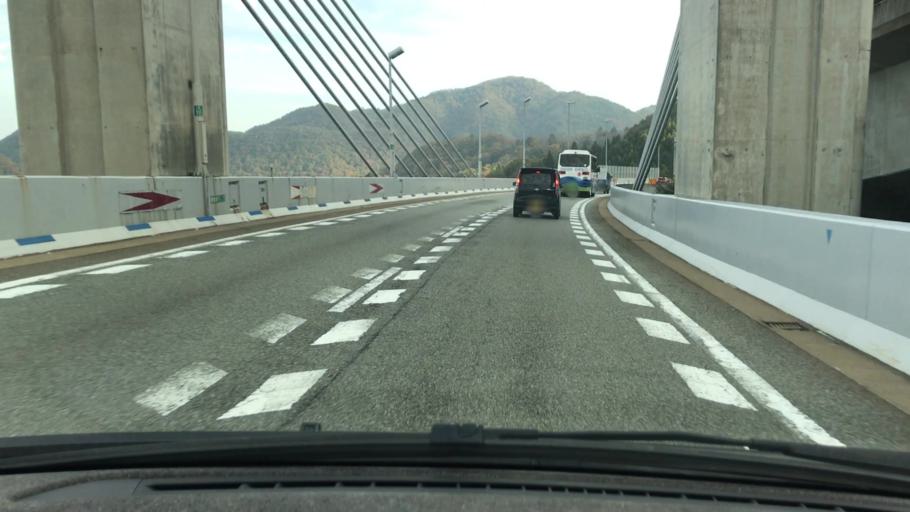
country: JP
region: Hyogo
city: Sandacho
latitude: 34.7881
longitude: 135.2195
